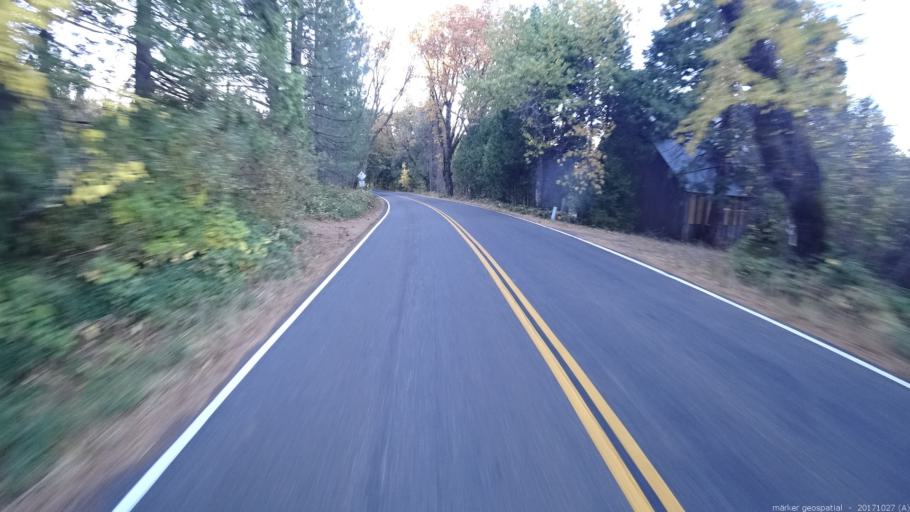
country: US
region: California
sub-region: Shasta County
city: Burney
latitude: 40.9071
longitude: -121.9044
